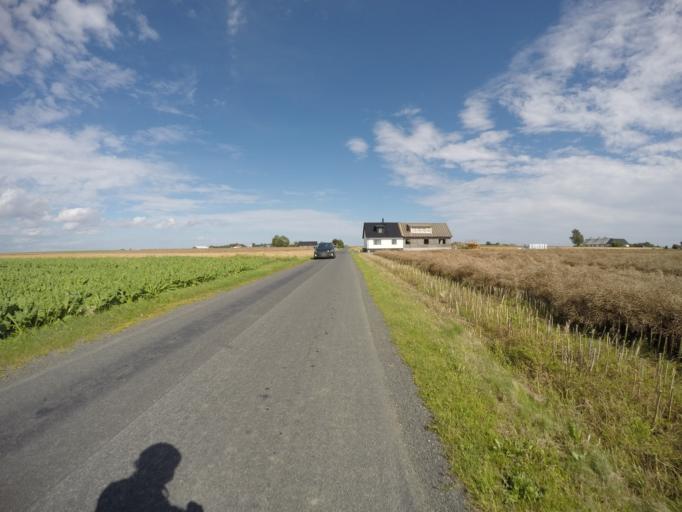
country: SE
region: Skane
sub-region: Simrishamns Kommun
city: Simrishamn
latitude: 55.4856
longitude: 14.1789
